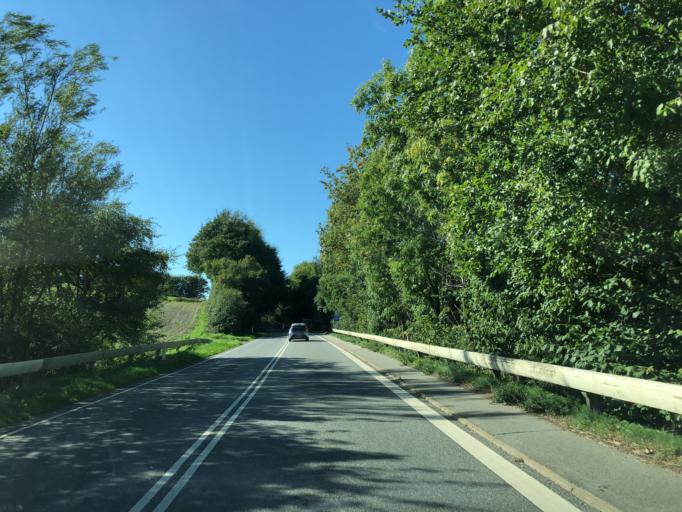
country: DK
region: South Denmark
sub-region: Aabenraa Kommune
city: Aabenraa
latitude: 55.0161
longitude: 9.4685
